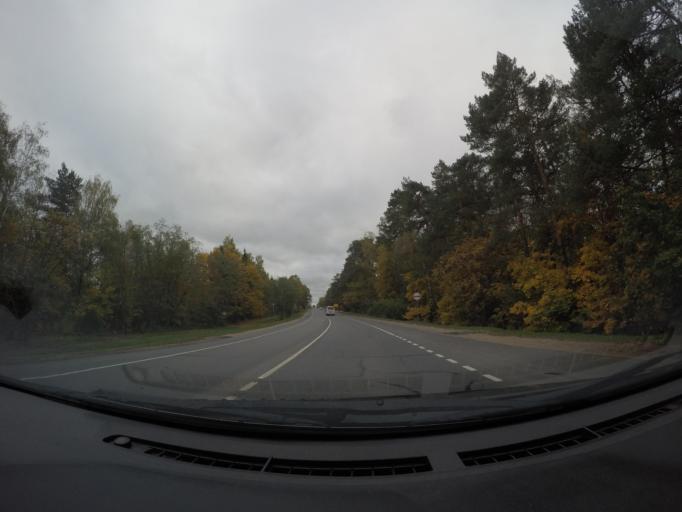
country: RU
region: Moskovskaya
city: Dorokhovo
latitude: 55.6391
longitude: 36.3280
